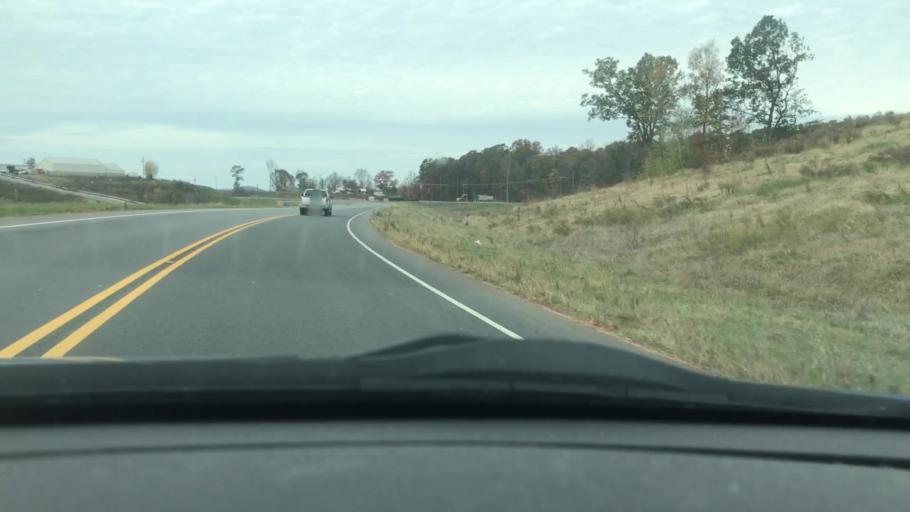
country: US
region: North Carolina
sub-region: Randolph County
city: Asheboro
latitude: 35.6986
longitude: -79.8719
